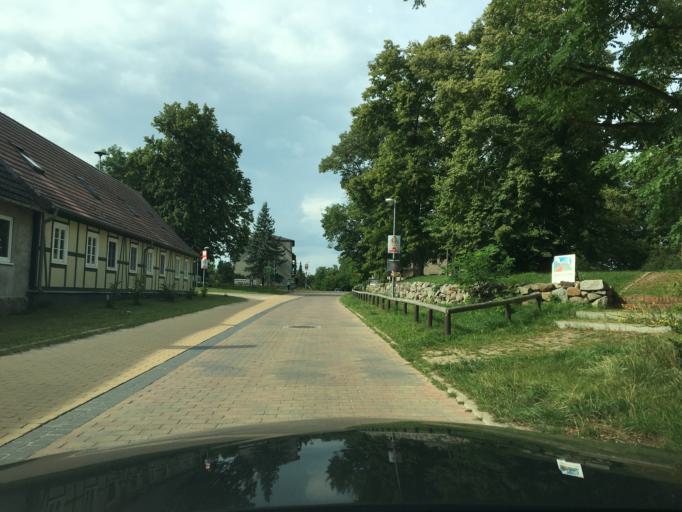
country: DE
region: Mecklenburg-Vorpommern
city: Waren
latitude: 53.4821
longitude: 12.7616
